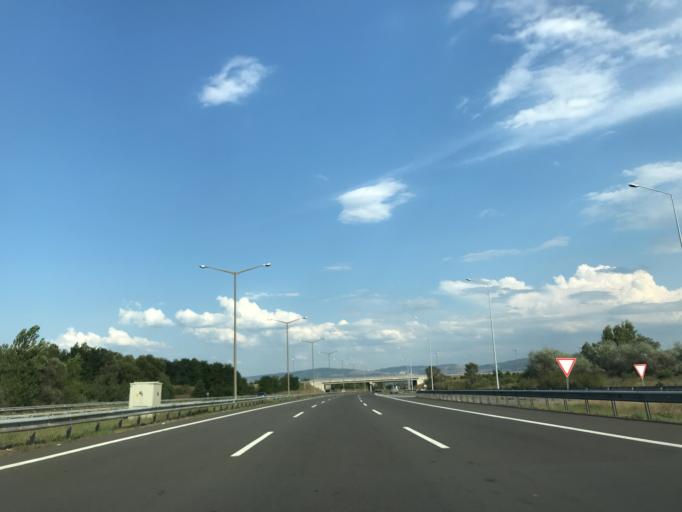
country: TR
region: Bolu
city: Gerede
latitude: 40.7386
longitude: 32.1892
